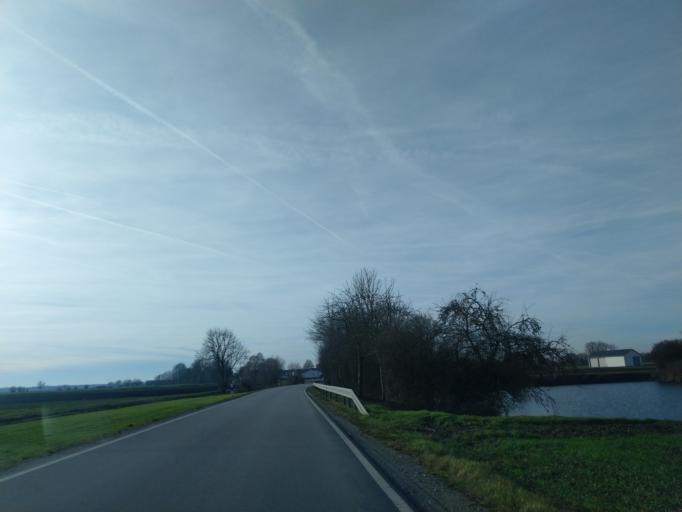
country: DE
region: Bavaria
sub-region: Lower Bavaria
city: Otzing
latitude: 48.7325
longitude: 12.7859
